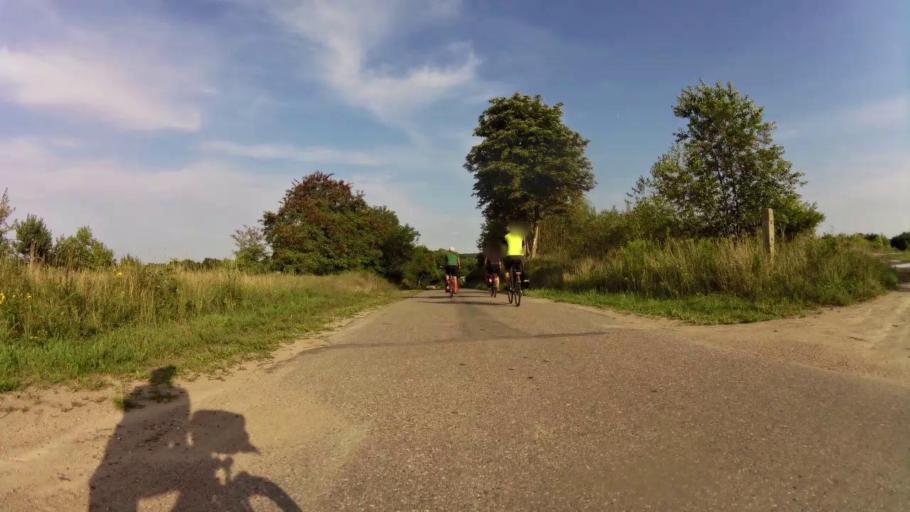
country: PL
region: West Pomeranian Voivodeship
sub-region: Powiat drawski
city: Drawsko Pomorskie
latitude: 53.4911
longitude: 15.7881
